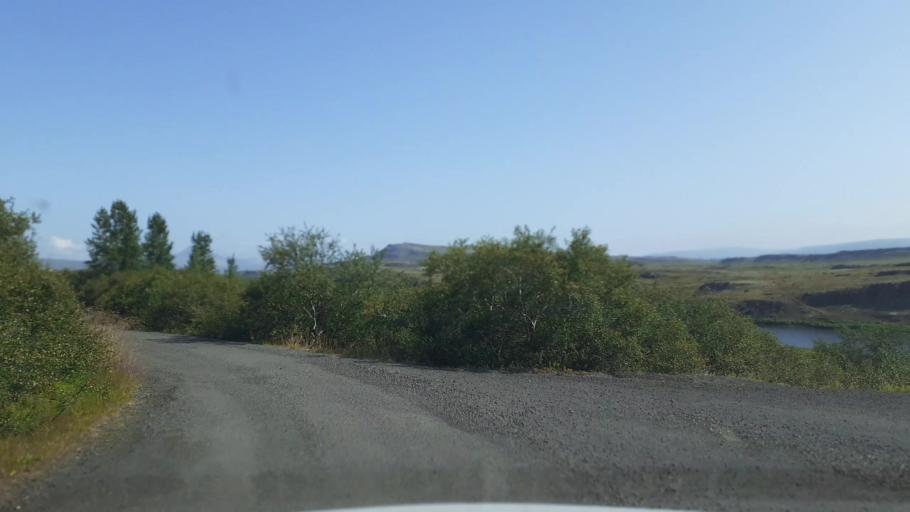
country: IS
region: West
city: Borgarnes
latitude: 64.7010
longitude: -21.6166
